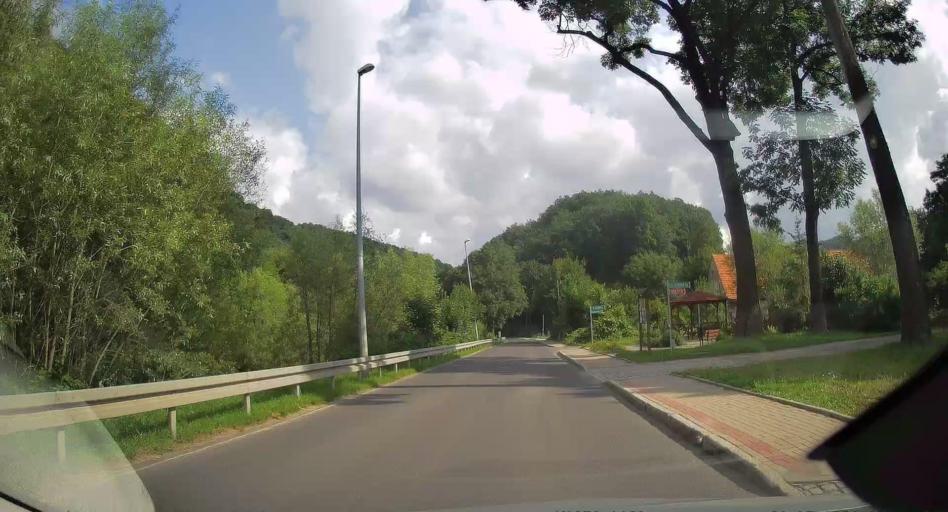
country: PL
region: Lower Silesian Voivodeship
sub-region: Powiat walbrzyski
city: Walim
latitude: 50.7347
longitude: 16.4041
